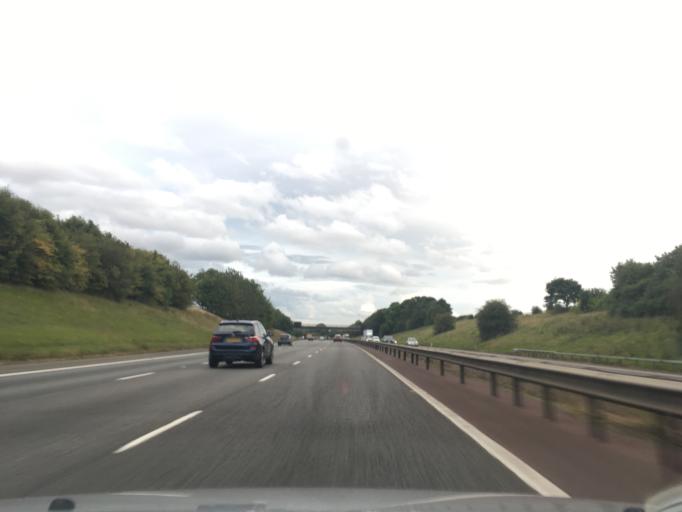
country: GB
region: England
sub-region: Oxfordshire
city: Adderbury
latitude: 52.0238
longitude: -1.2947
